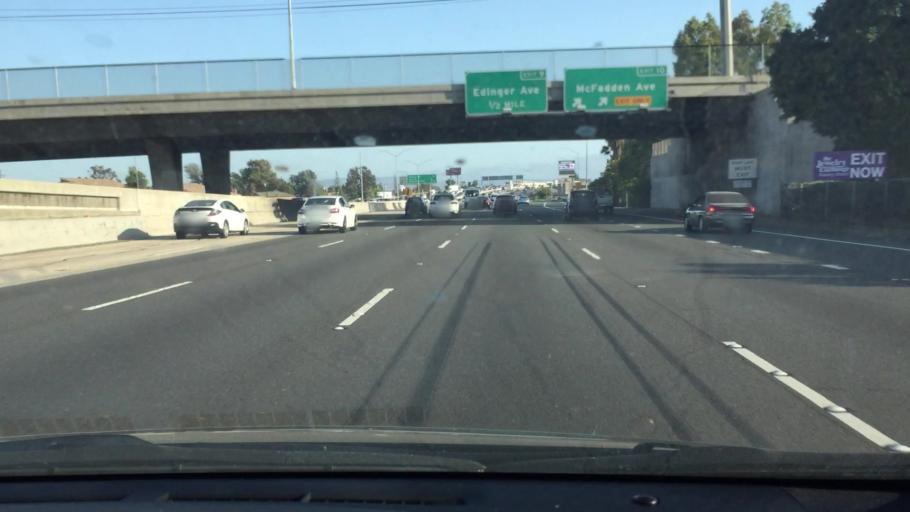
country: US
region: California
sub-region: Orange County
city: Tustin
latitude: 33.7344
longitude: -117.8340
